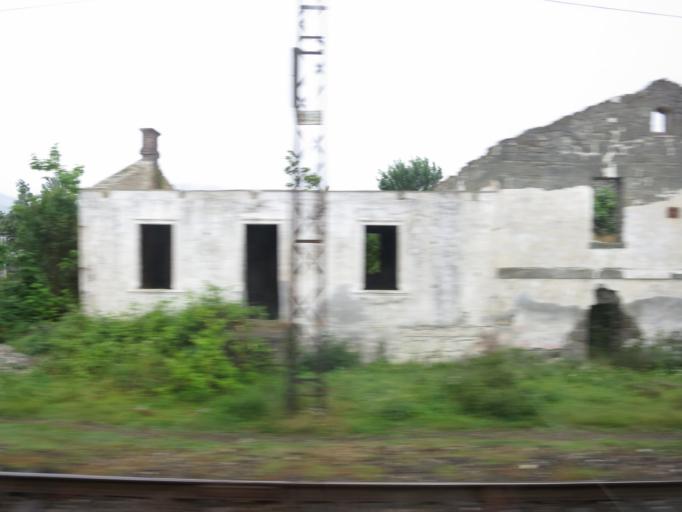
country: GE
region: Guria
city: Lanchkhuti
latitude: 42.0913
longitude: 42.0470
